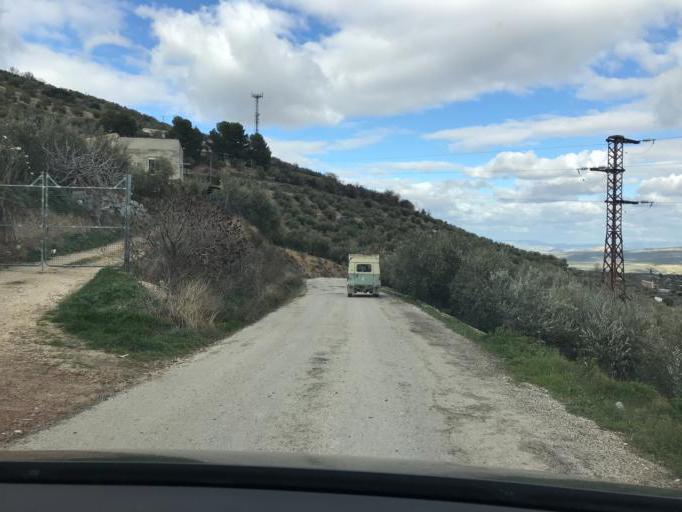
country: ES
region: Andalusia
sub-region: Provincia de Jaen
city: Torres
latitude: 37.7975
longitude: -3.4657
